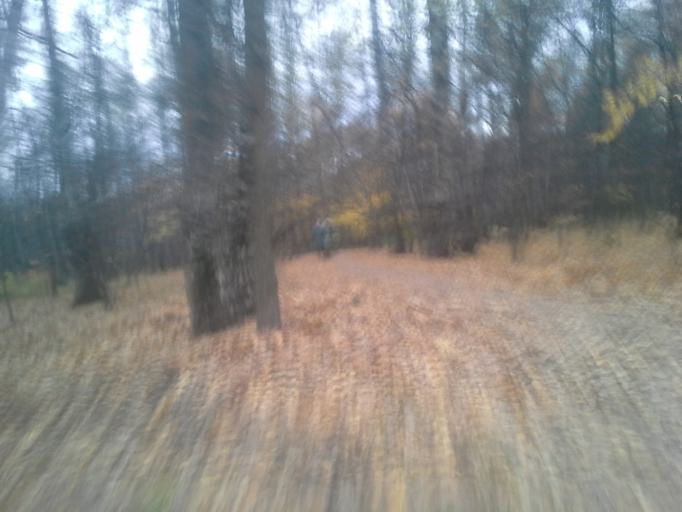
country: RU
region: Moscow
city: Solntsevo
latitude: 55.6614
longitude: 37.3711
